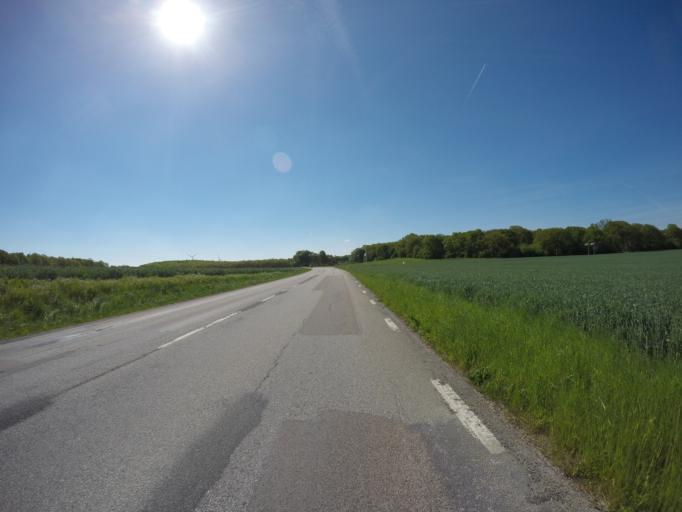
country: SE
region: Skane
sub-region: Malmo
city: Oxie
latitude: 55.5340
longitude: 13.1323
